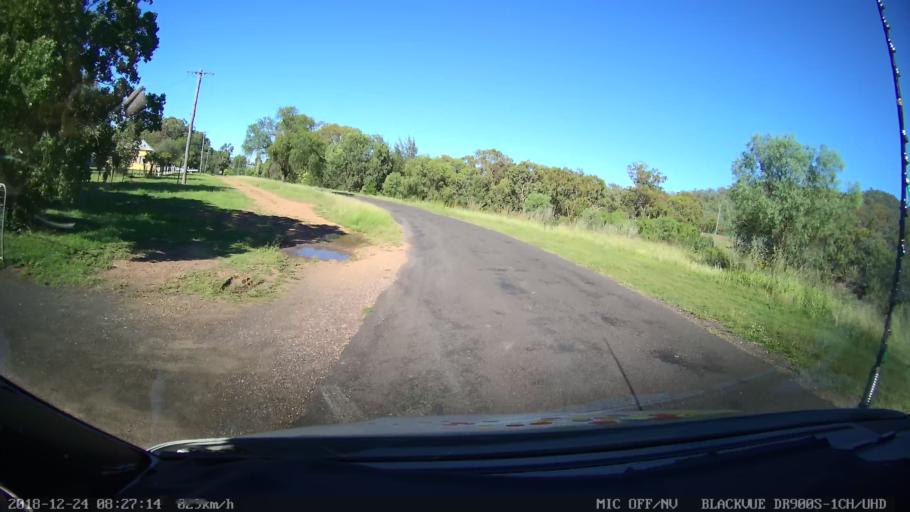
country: AU
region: New South Wales
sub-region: Tamworth Municipality
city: Phillip
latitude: -31.2604
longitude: 150.7377
